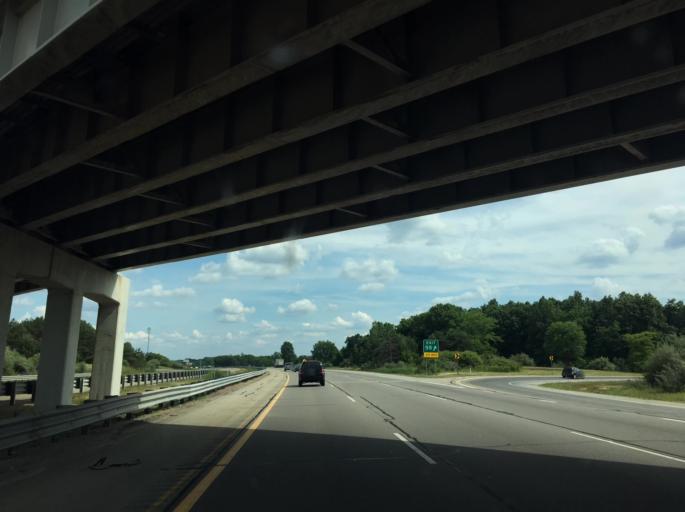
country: US
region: Michigan
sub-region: Oakland County
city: Holly
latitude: 42.7824
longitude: -83.5350
